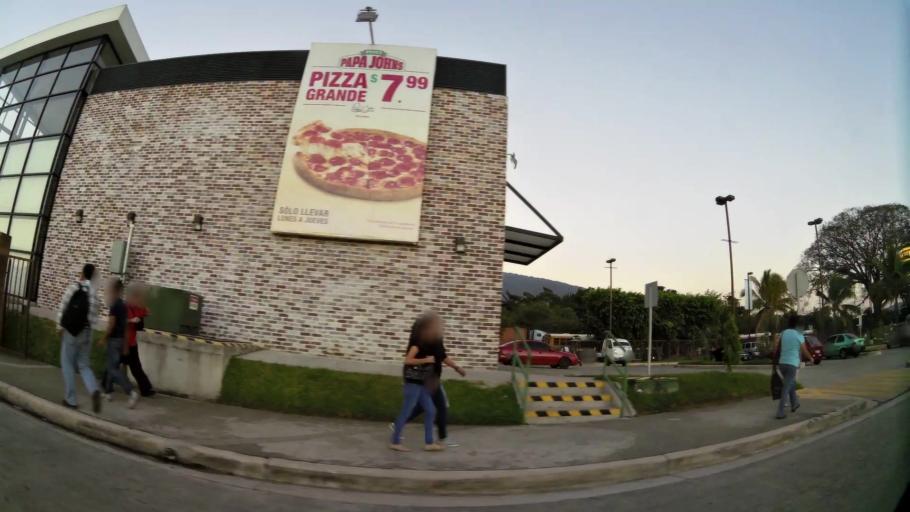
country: SV
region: La Libertad
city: Santa Tecla
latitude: 13.7297
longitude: -89.3595
